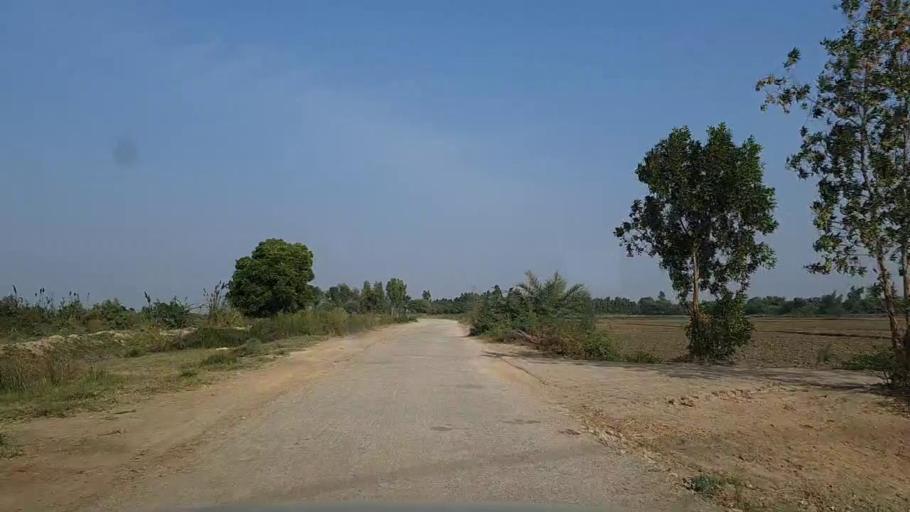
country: PK
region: Sindh
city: Mirpur Sakro
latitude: 24.5965
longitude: 67.5875
